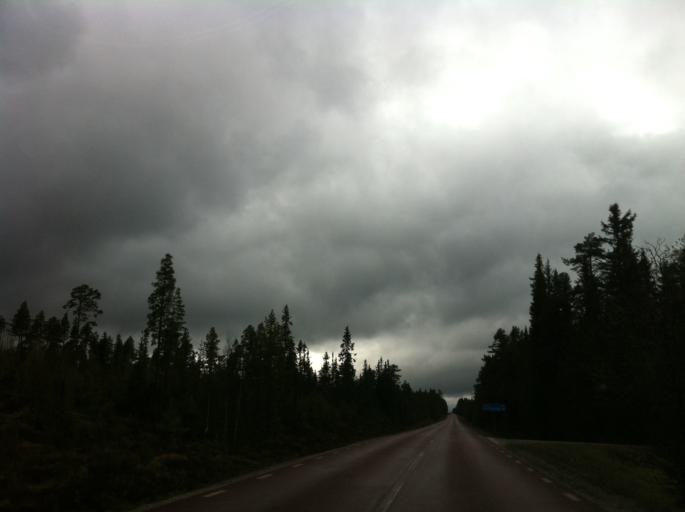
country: NO
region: Hedmark
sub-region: Engerdal
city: Engerdal
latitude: 62.4363
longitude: 12.7135
